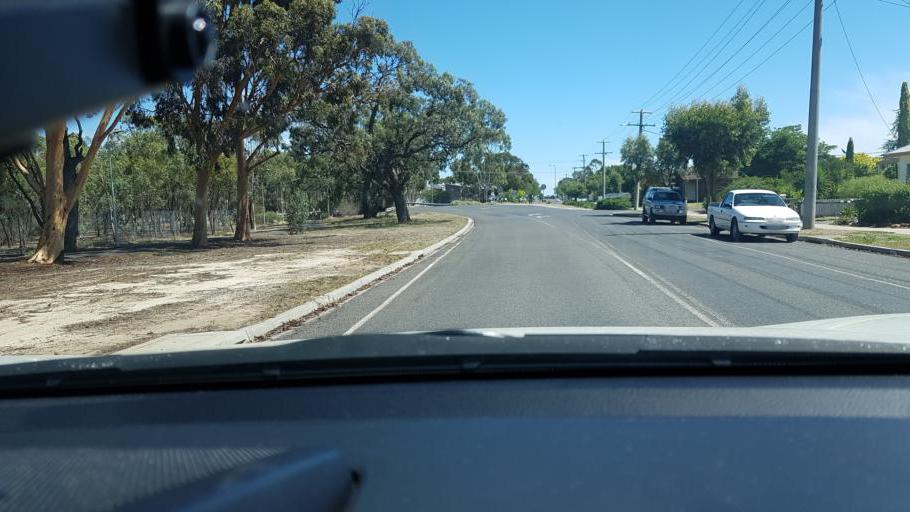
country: AU
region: Victoria
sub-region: Horsham
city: Horsham
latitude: -36.7118
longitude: 142.1891
